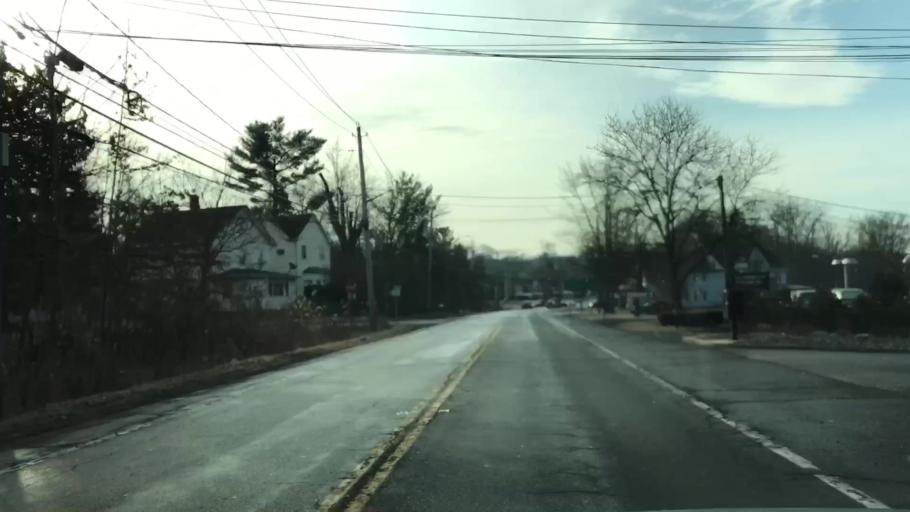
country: US
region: New York
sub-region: Rockland County
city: Congers
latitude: 41.1489
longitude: -73.9347
